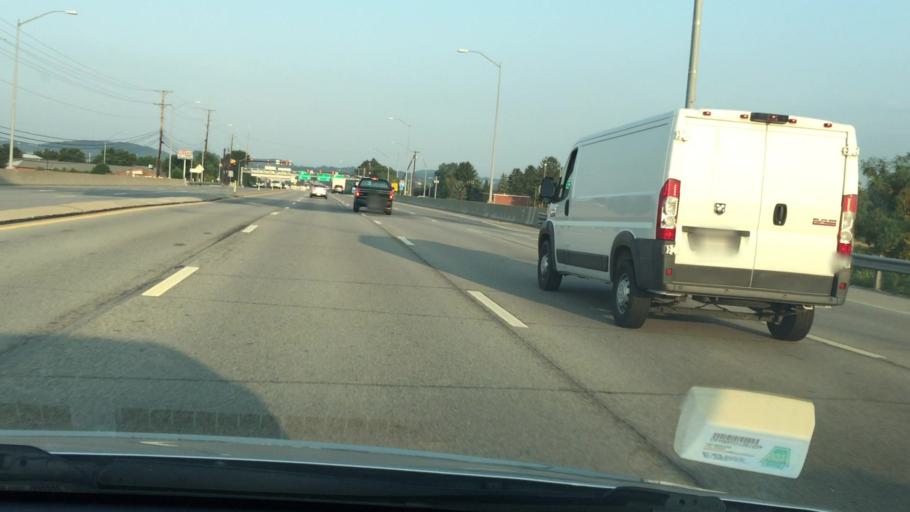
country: US
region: Pennsylvania
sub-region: Butler County
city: Cranberry Township
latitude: 40.6854
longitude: -80.0944
